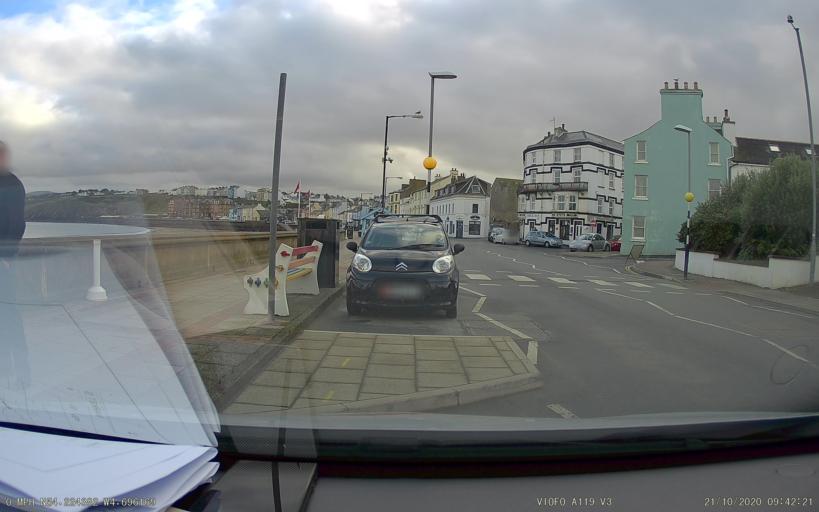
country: IM
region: Port Erin
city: Port Erin
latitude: 54.2120
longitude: -4.6962
